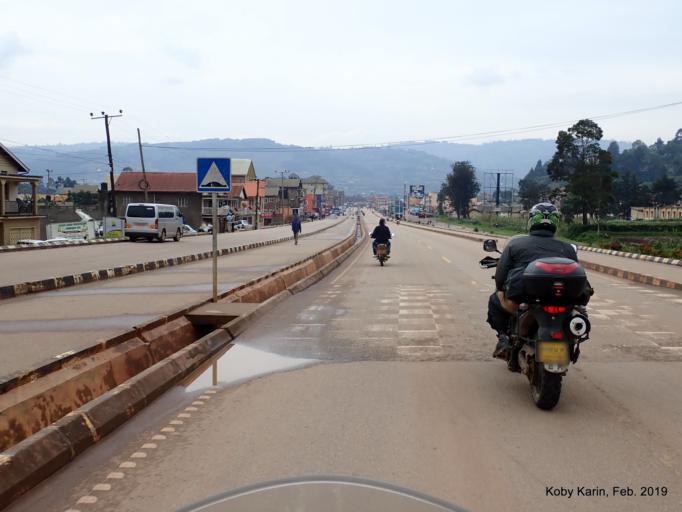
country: UG
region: Western Region
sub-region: Kabale District
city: Kabale
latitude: -1.2554
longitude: 30.0005
